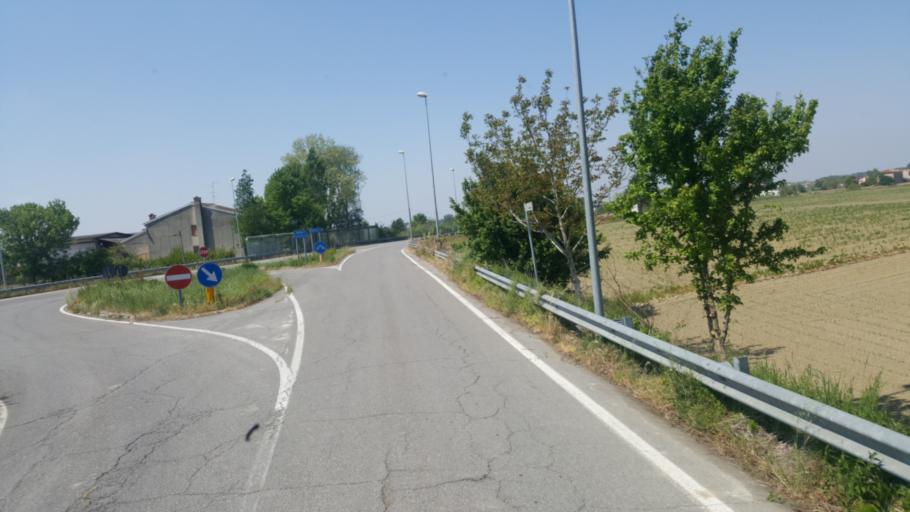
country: IT
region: Lombardy
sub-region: Provincia di Mantova
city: Quistello
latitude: 44.9951
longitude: 11.0024
